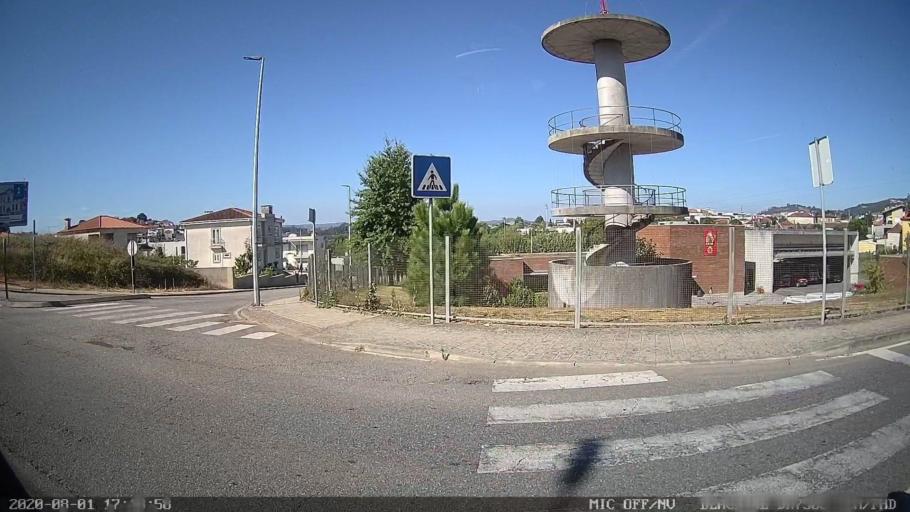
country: PT
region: Porto
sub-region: Santo Tirso
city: Santo Tirso
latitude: 41.3392
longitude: -8.4866
